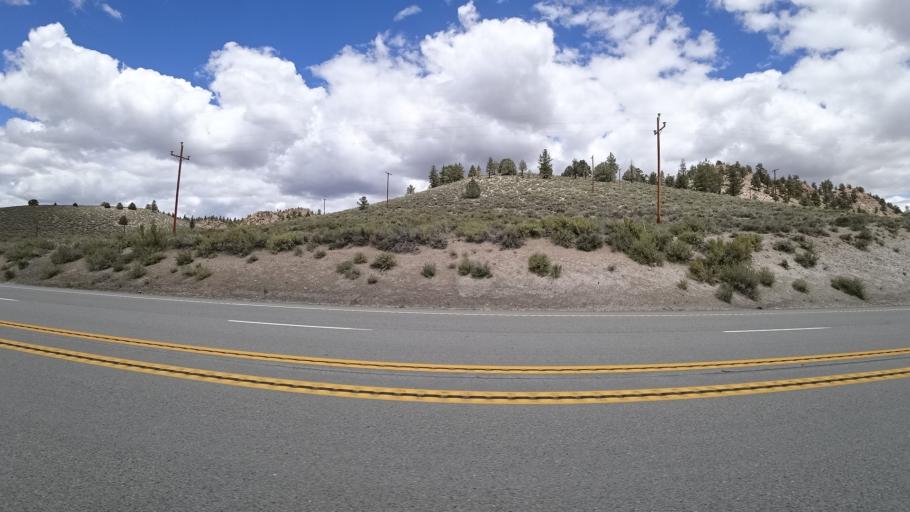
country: US
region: California
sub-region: Inyo County
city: West Bishop
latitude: 37.5541
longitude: -118.6468
